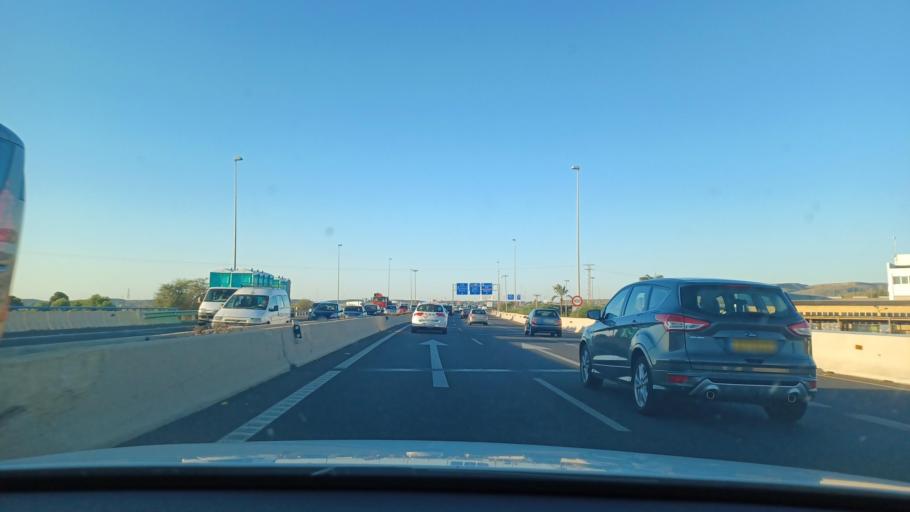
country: ES
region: Valencia
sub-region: Provincia de Alicante
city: San Vicent del Raspeig
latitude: 38.3438
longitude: -0.5419
